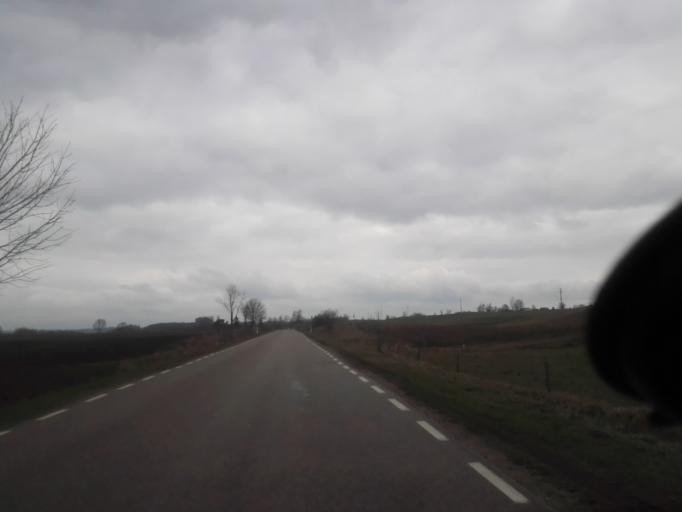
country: PL
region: Podlasie
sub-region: Suwalki
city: Suwalki
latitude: 54.2279
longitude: 22.9122
